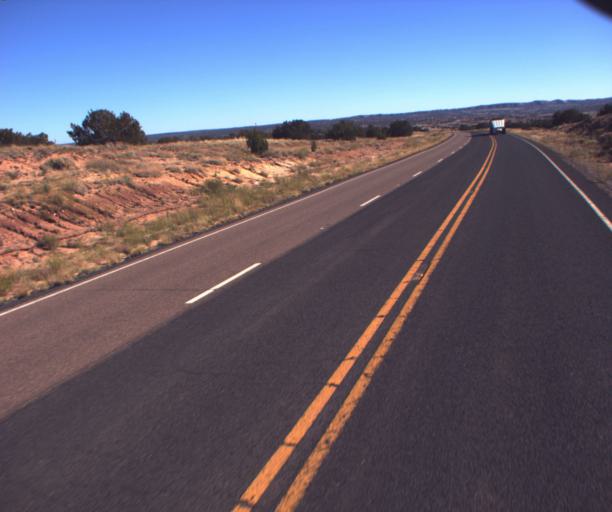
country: US
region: Arizona
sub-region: Apache County
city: Ganado
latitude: 35.4141
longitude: -109.5129
